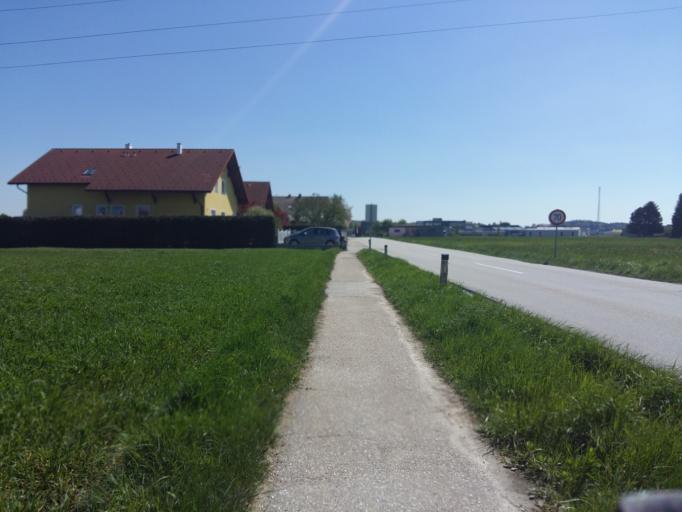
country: AT
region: Upper Austria
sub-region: Politischer Bezirk Scharding
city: Sankt Marienkirchen bei Schaerding
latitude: 48.3935
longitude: 13.4450
